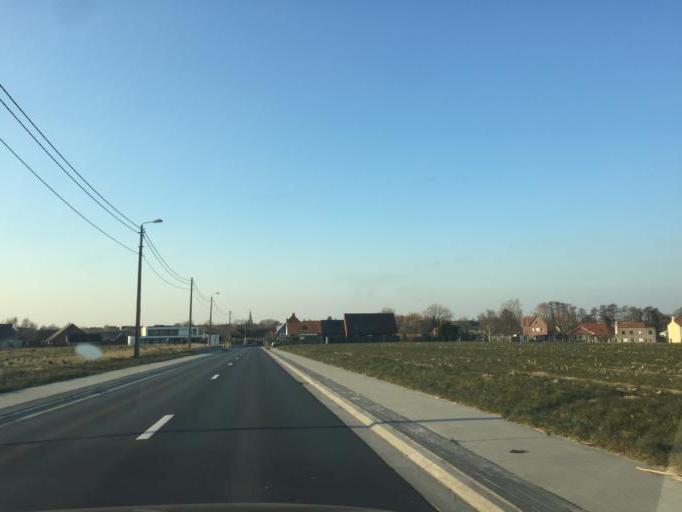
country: BE
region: Flanders
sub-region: Provincie West-Vlaanderen
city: Meulebeke
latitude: 50.9394
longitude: 3.2962
